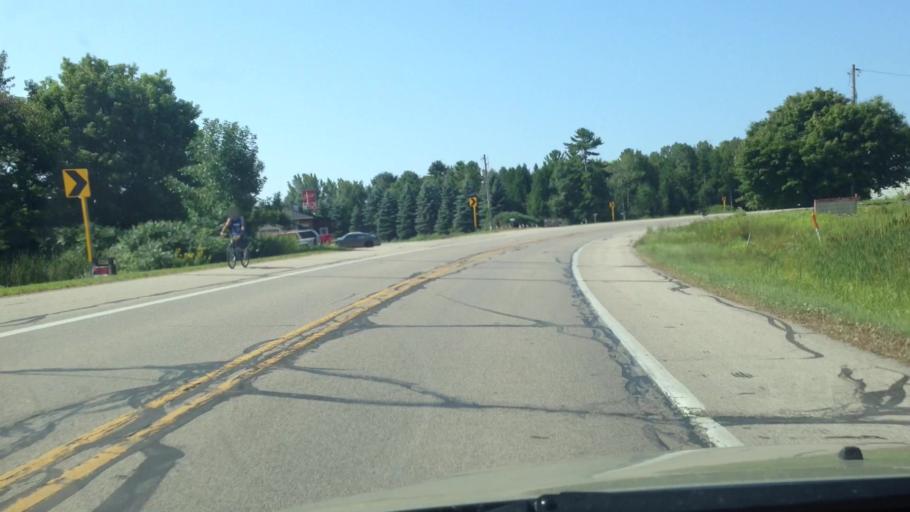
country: US
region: Michigan
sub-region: Delta County
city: Escanaba
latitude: 45.6892
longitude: -87.1010
